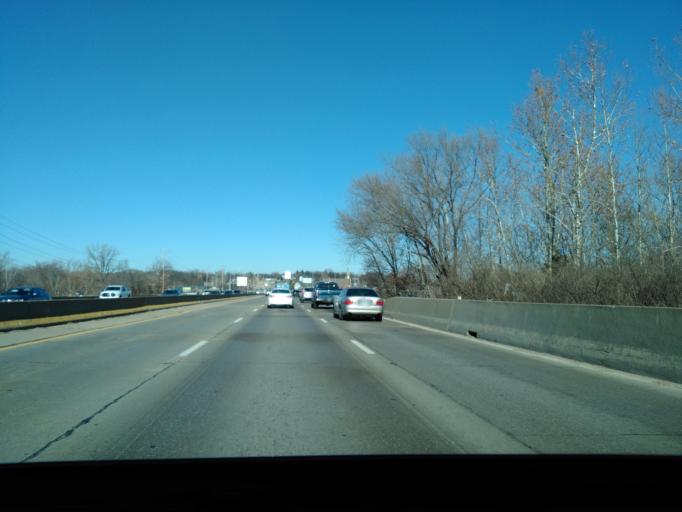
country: US
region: Missouri
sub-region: Saint Louis County
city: Valley Park
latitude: 38.5455
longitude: -90.4946
